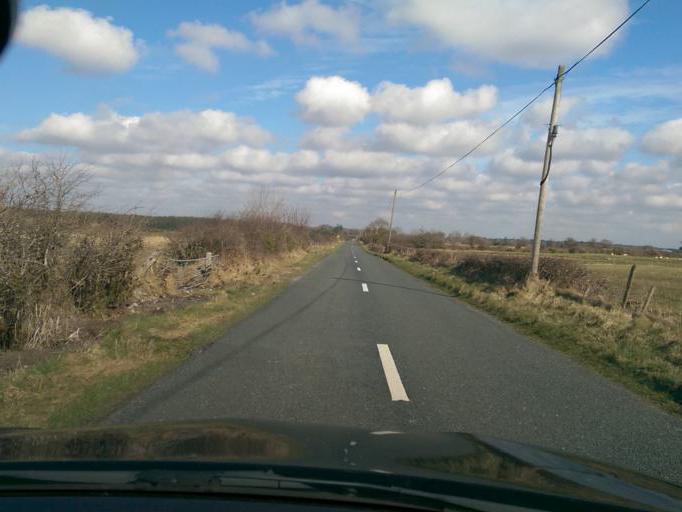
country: IE
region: Connaught
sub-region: County Galway
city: Athenry
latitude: 53.4471
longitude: -8.5573
